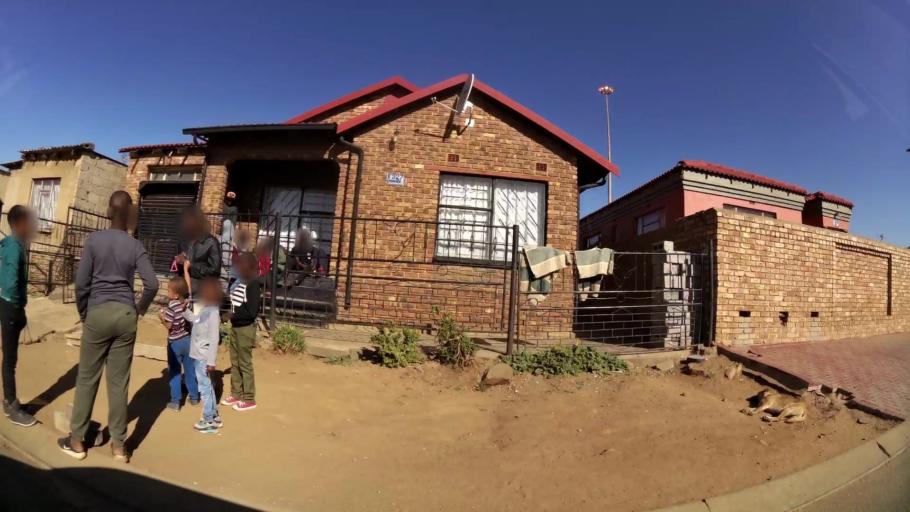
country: ZA
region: Gauteng
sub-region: Ekurhuleni Metropolitan Municipality
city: Tembisa
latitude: -26.0179
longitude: 28.2340
